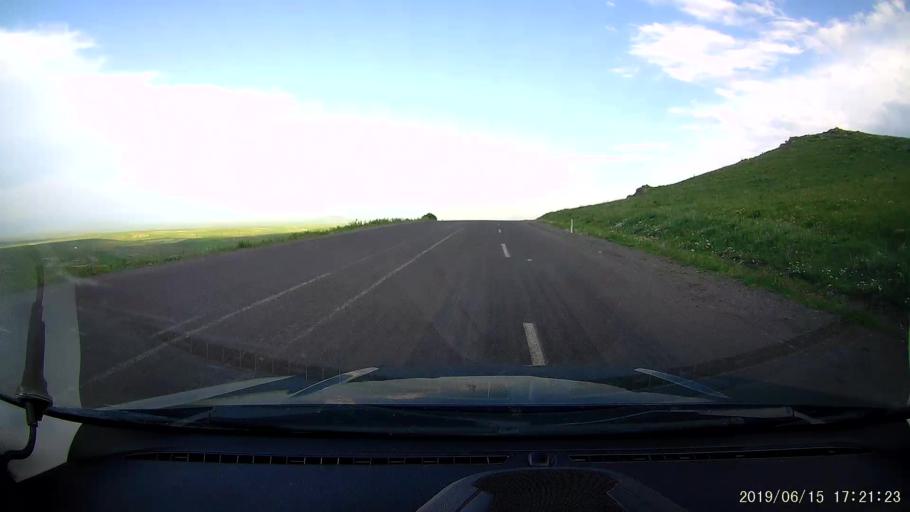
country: TR
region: Kars
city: Basgedikler
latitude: 40.6176
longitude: 43.3235
